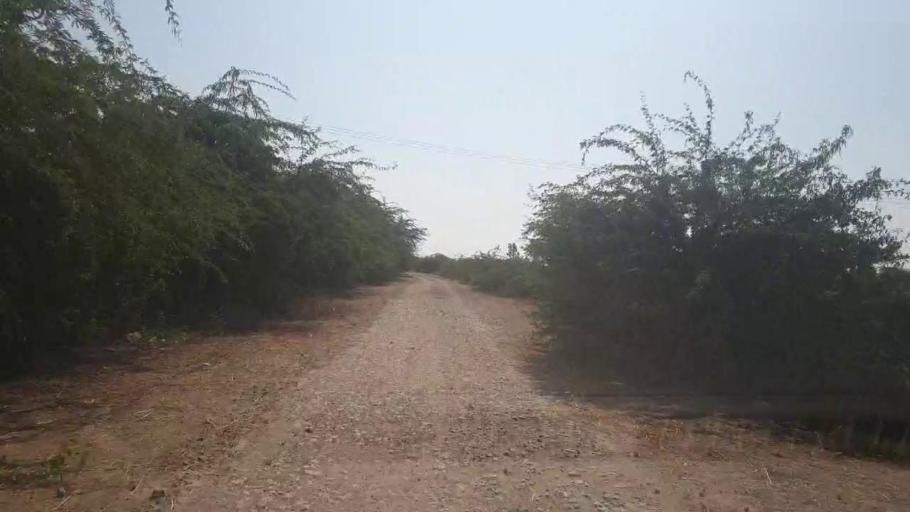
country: PK
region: Sindh
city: Badin
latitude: 24.5805
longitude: 68.8462
